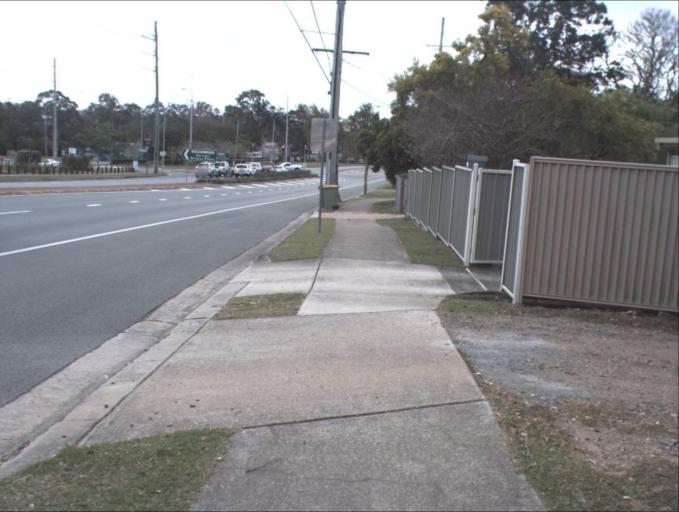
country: AU
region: Queensland
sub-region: Logan
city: Waterford West
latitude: -27.6788
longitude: 153.1216
